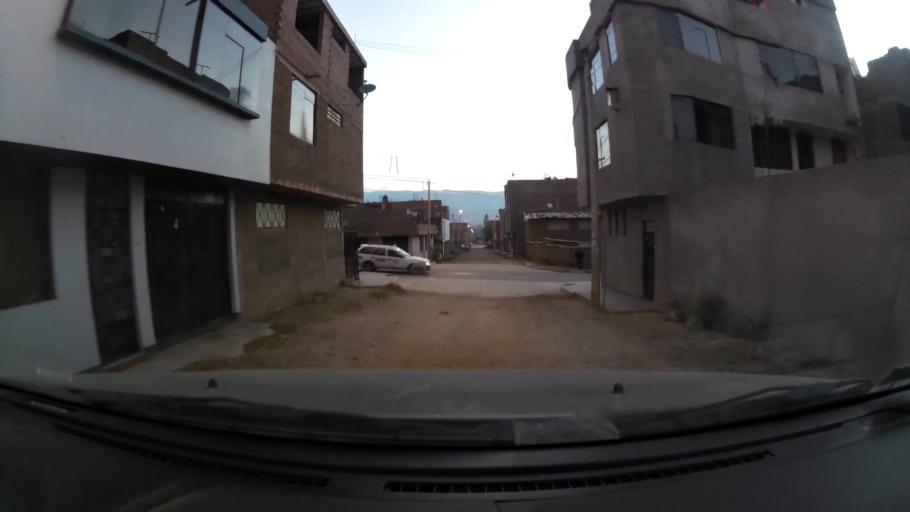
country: PE
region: Junin
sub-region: Provincia de Huancayo
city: El Tambo
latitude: -12.0609
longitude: -75.2308
